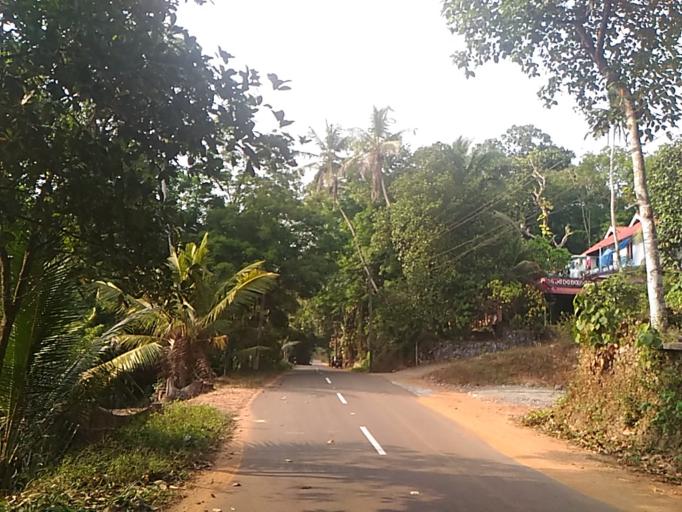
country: IN
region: Kerala
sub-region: Kottayam
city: Palackattumala
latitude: 9.7801
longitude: 76.6738
